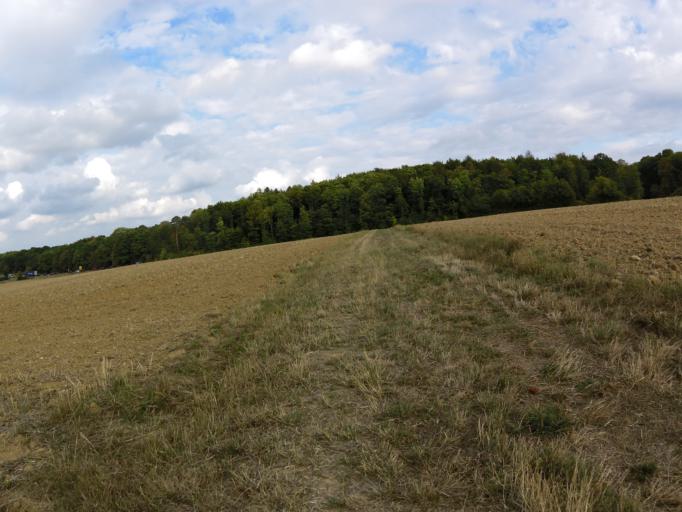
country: DE
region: Bavaria
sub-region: Regierungsbezirk Unterfranken
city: Kist
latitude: 49.7555
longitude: 9.8466
